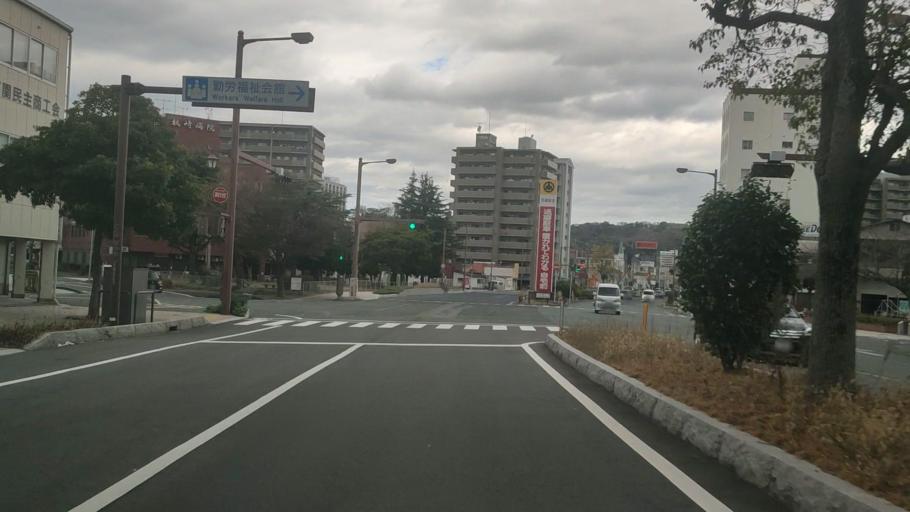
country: JP
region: Yamaguchi
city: Shimonoseki
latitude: 33.9601
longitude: 130.9418
